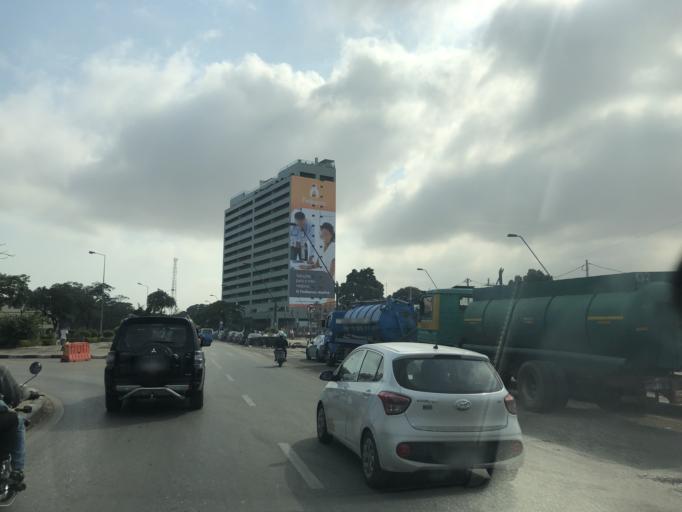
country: AO
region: Luanda
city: Luanda
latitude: -8.8385
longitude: 13.2357
